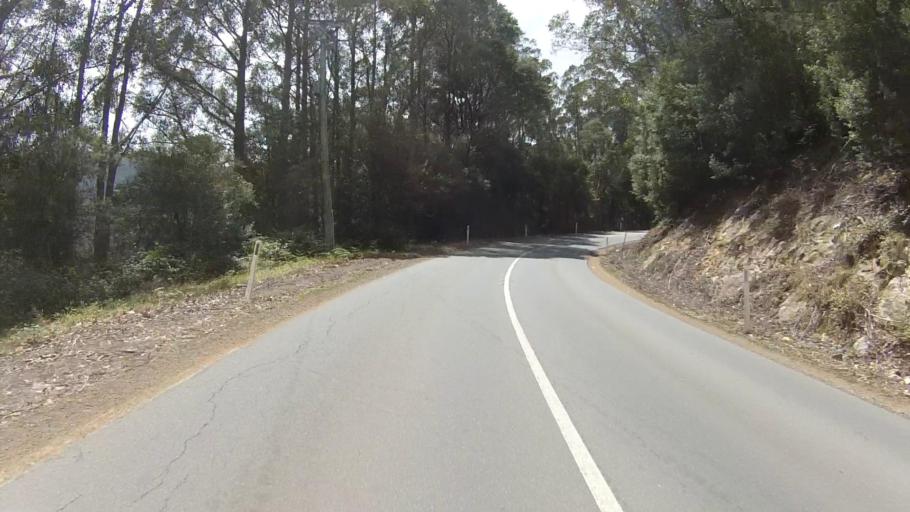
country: AU
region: Tasmania
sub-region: Kingborough
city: Kettering
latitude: -43.1265
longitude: 147.1681
